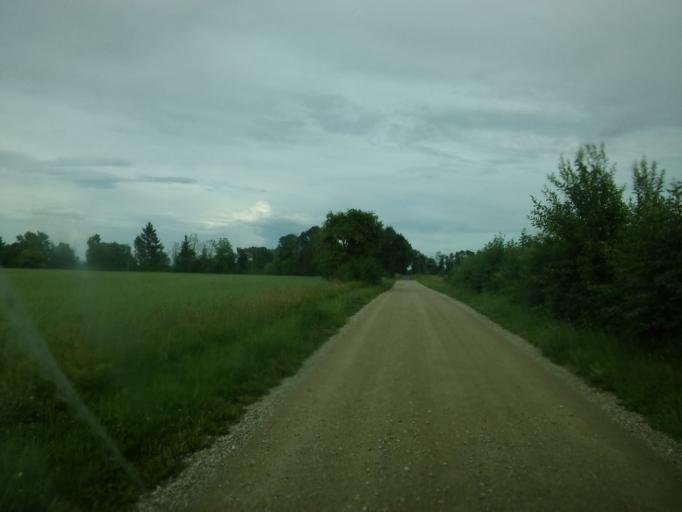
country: EE
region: Raplamaa
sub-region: Rapla vald
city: Rapla
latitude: 58.9002
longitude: 24.7696
